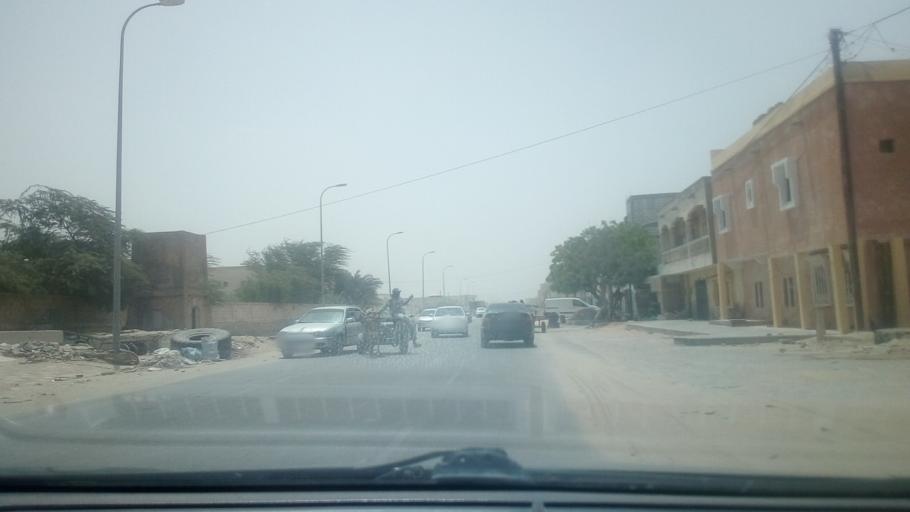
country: MR
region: Nouakchott
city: Nouakchott
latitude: 18.0760
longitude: -15.9851
